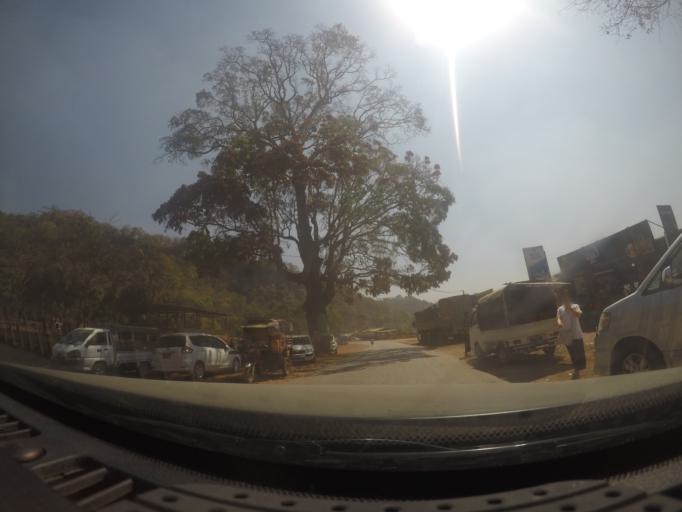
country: MM
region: Shan
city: Taunggyi
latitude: 20.8177
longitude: 97.2216
